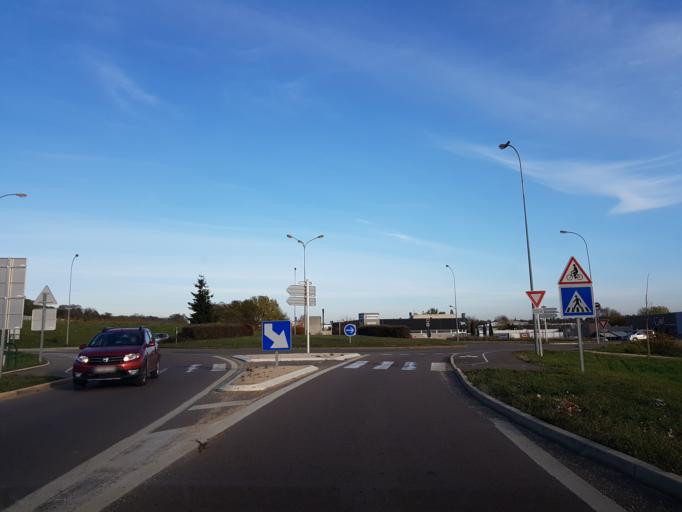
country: FR
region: Bourgogne
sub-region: Departement de la Cote-d'Or
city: Ahuy
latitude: 47.3578
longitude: 5.0333
